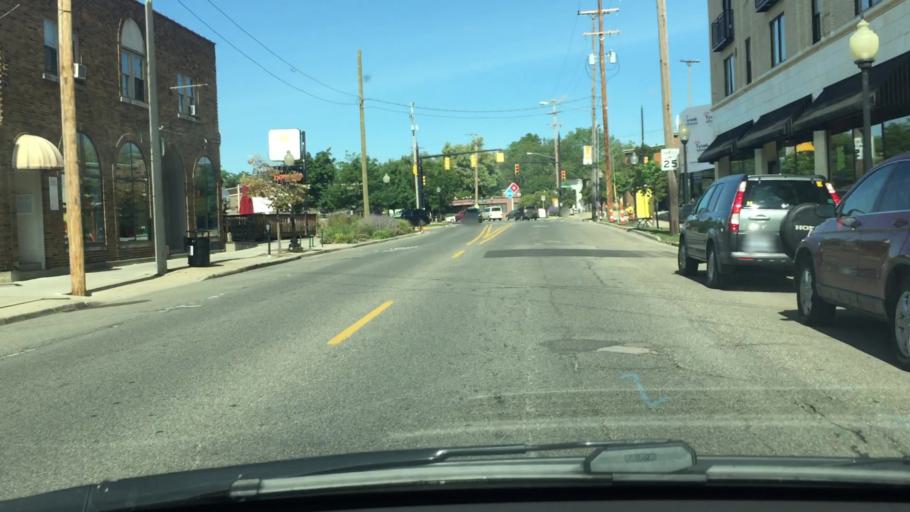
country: US
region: Michigan
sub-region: Kent County
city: East Grand Rapids
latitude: 42.9570
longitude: -85.6342
